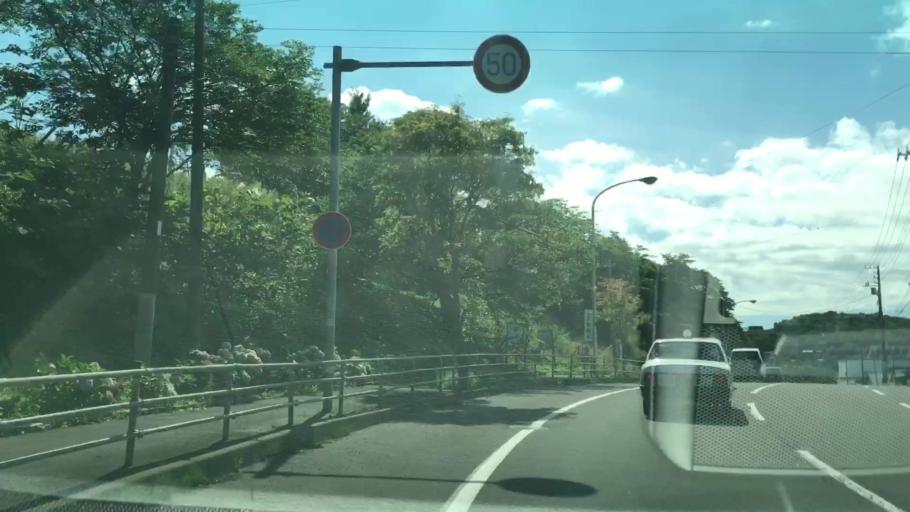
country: JP
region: Hokkaido
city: Muroran
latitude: 42.3181
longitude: 140.9952
